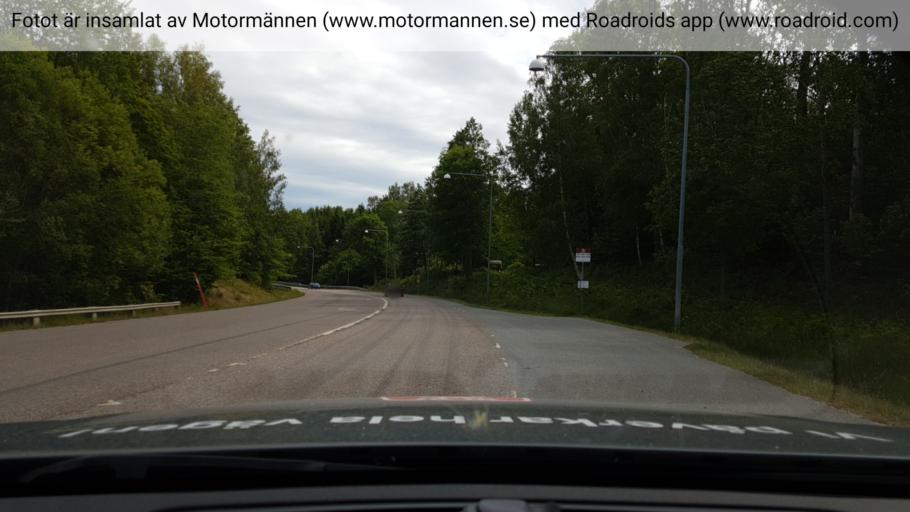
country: SE
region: Stockholm
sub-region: Nynashamns Kommun
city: Nynashamn
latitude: 58.9204
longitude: 17.9242
